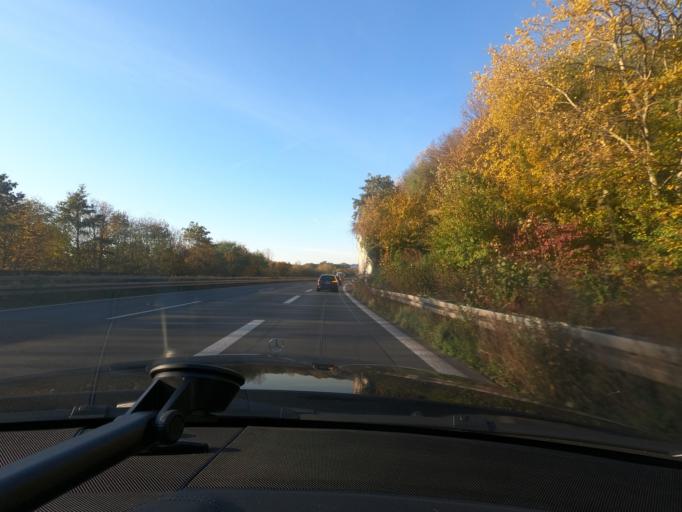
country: DE
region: North Rhine-Westphalia
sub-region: Regierungsbezirk Dusseldorf
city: Dinslaken
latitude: 51.5359
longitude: 6.7503
